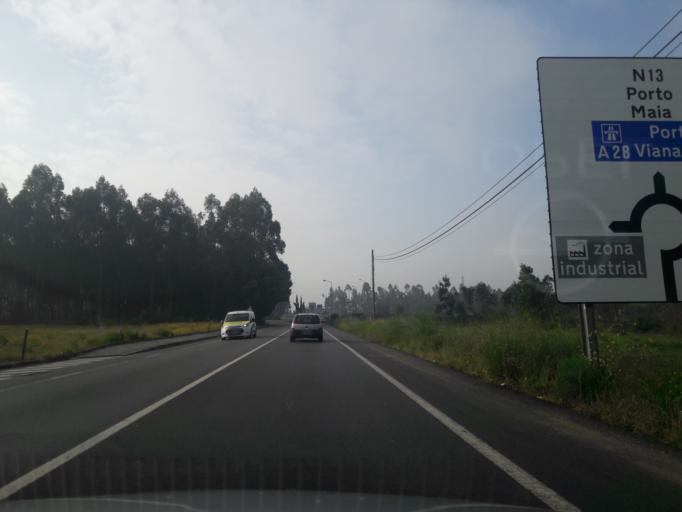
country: PT
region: Porto
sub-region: Vila do Conde
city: Arvore
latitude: 41.3063
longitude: -8.7033
